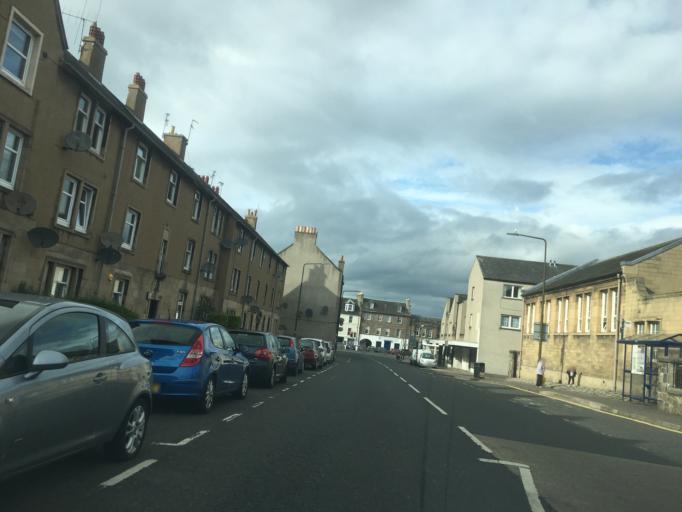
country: GB
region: Scotland
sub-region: East Lothian
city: Musselburgh
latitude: 55.9421
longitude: -3.0477
